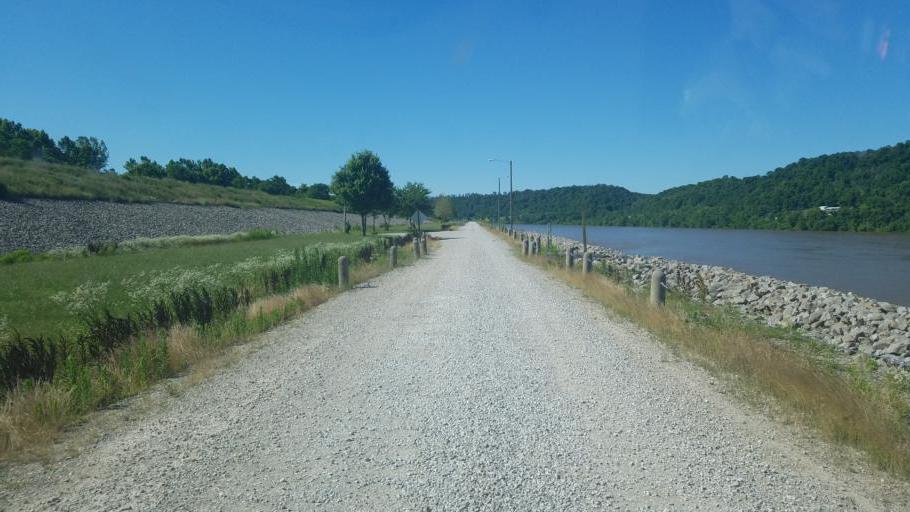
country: US
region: Ohio
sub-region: Gallia County
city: Gallipolis
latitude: 38.6767
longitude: -82.1832
